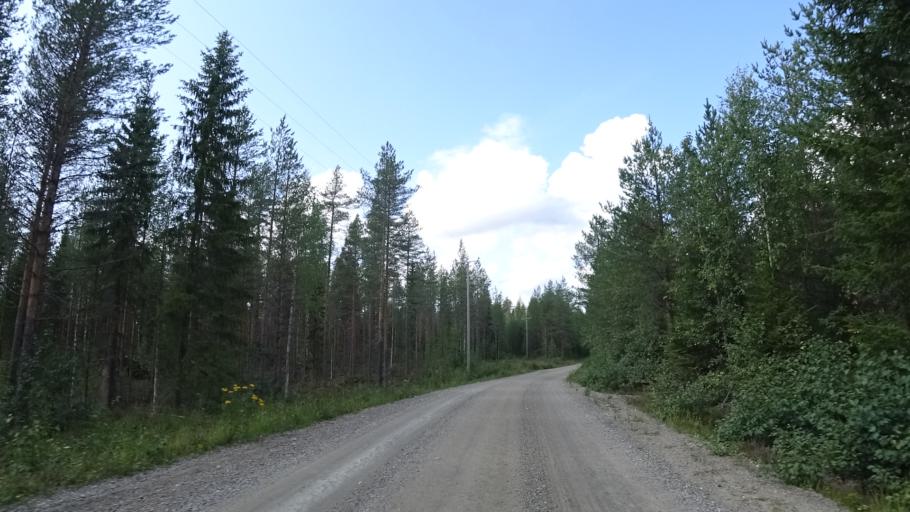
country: FI
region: North Karelia
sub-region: Joensuu
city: Ilomantsi
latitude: 62.9279
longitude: 31.3264
